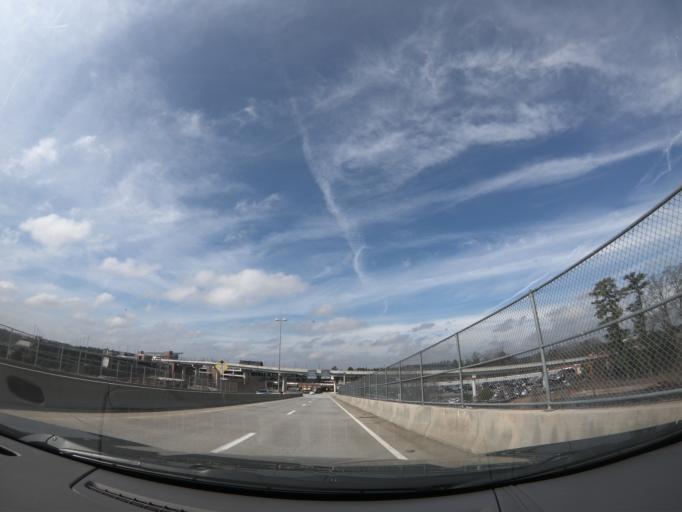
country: US
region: Georgia
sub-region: Fulton County
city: College Park
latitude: 33.6389
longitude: -84.4603
